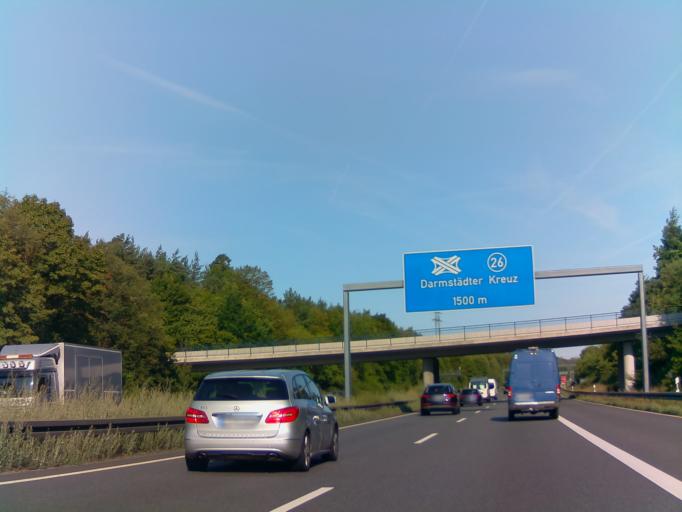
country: DE
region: Hesse
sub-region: Regierungsbezirk Darmstadt
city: Darmstadt
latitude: 49.8460
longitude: 8.6166
